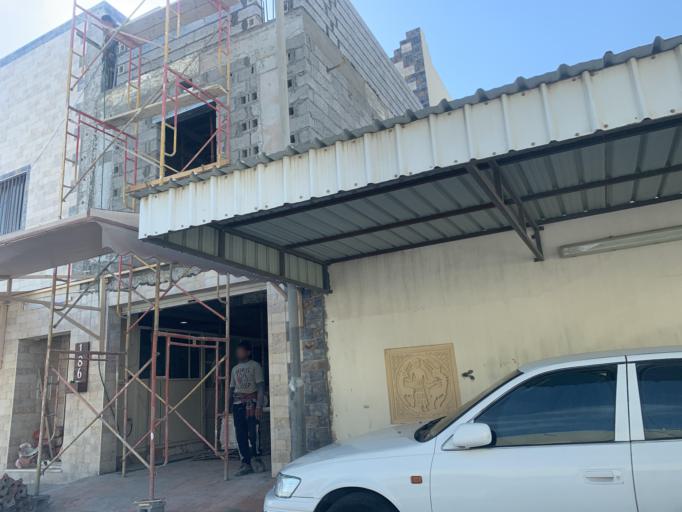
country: BH
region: Central Governorate
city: Madinat Hamad
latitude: 26.1279
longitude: 50.4969
